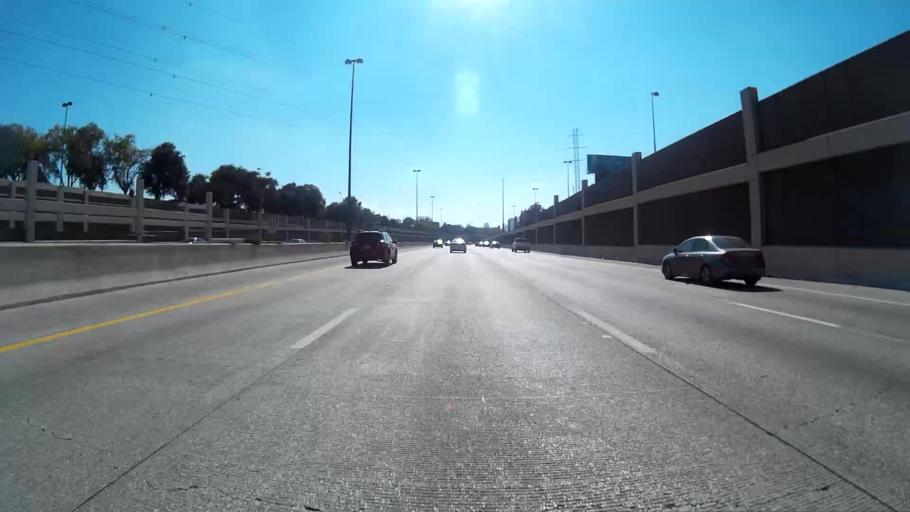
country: US
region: Texas
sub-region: Dallas County
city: Highland Park
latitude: 32.8339
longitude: -96.7802
